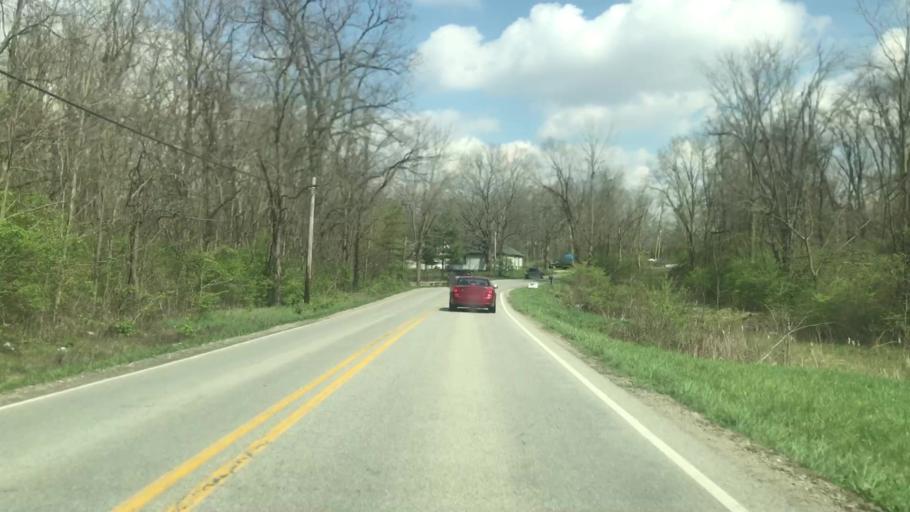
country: US
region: Indiana
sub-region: Johnson County
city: Waterloo
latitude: 39.5520
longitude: -86.2117
